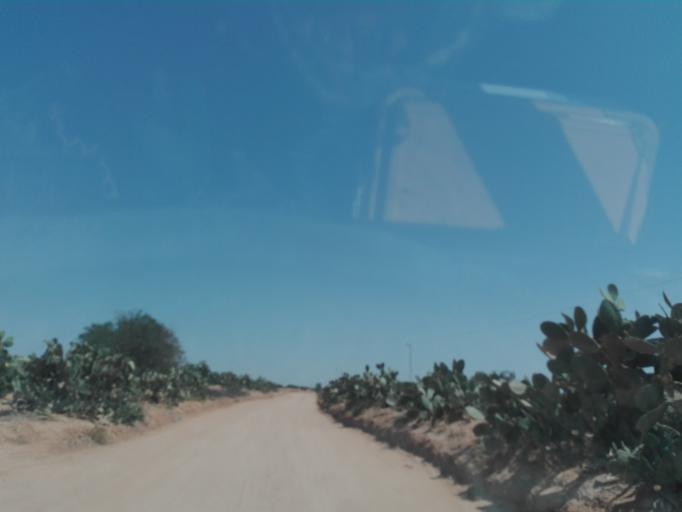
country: TN
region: Safaqis
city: Bi'r `Ali Bin Khalifah
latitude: 34.6659
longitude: 10.2380
